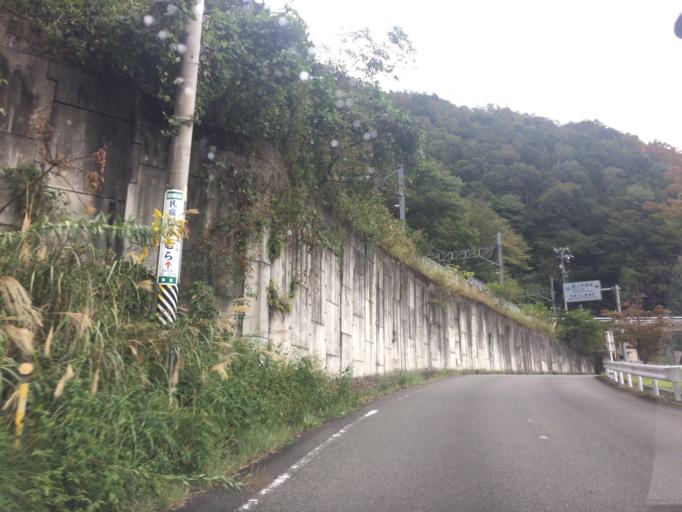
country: JP
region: Shizuoka
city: Shizuoka-shi
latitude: 35.1695
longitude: 138.1562
